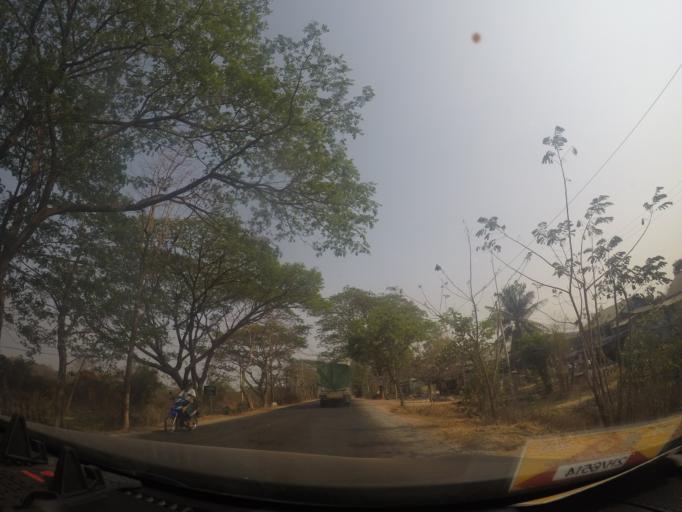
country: MM
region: Bago
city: Paungde
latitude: 18.4813
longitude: 95.5148
